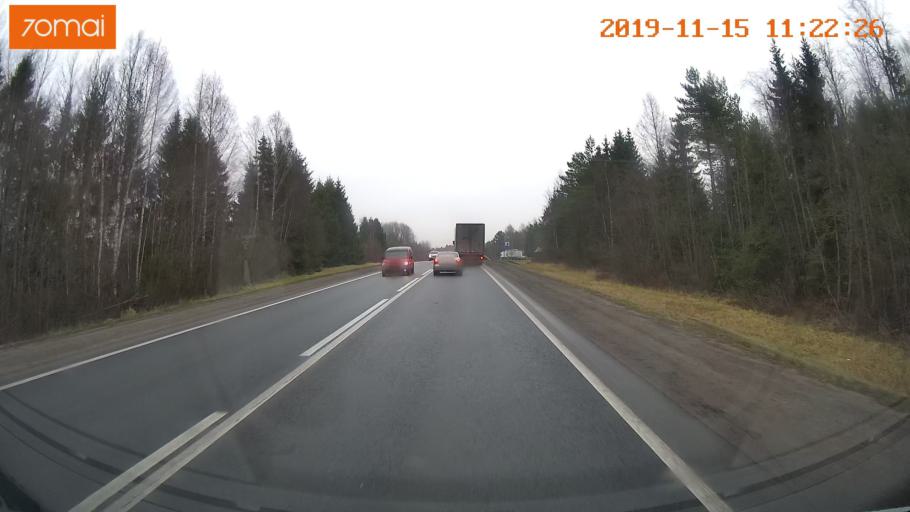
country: RU
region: Vologda
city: Molochnoye
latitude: 59.1477
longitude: 39.3625
